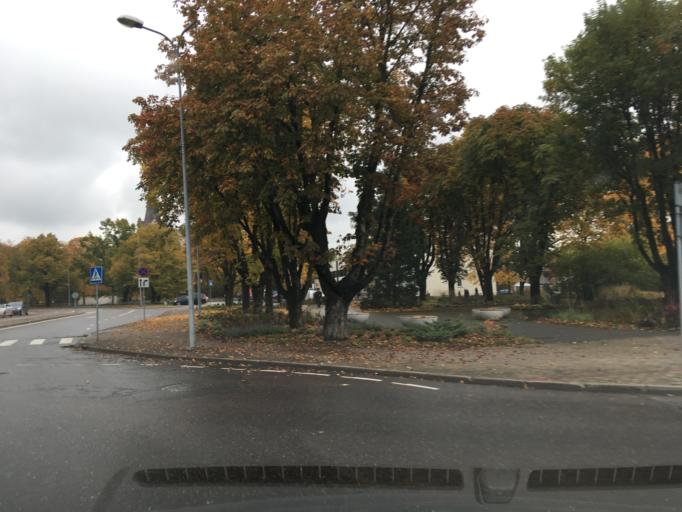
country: EE
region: Harju
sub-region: Keila linn
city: Keila
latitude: 59.3082
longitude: 24.4257
